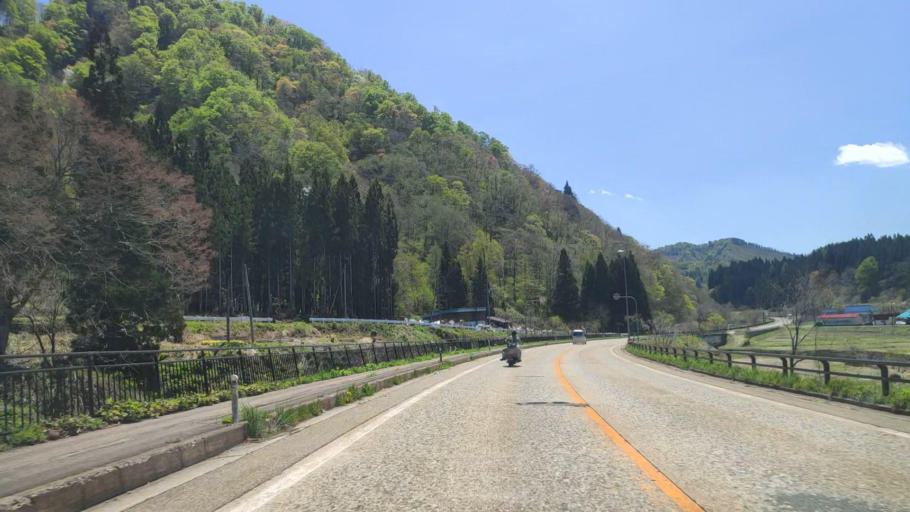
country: JP
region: Akita
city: Yuzawa
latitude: 38.9935
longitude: 140.3635
